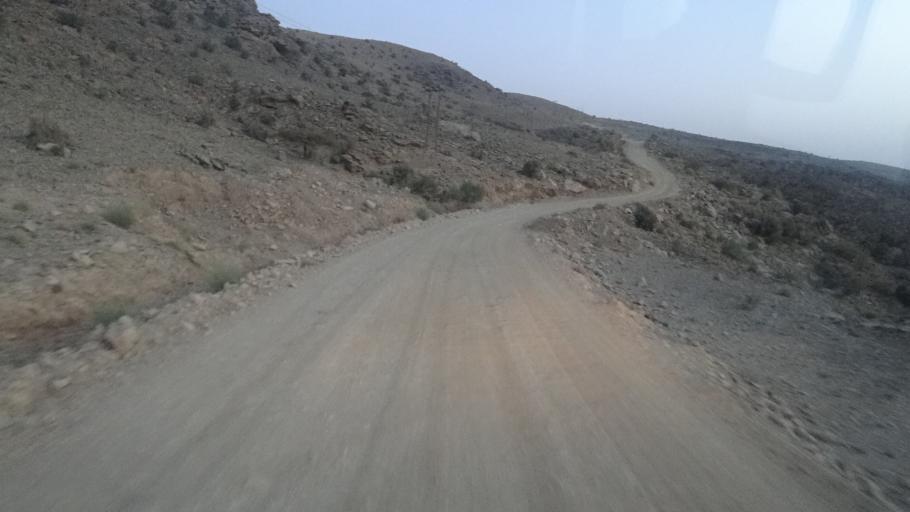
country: OM
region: Al Batinah
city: Rustaq
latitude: 23.2434
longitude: 57.1684
